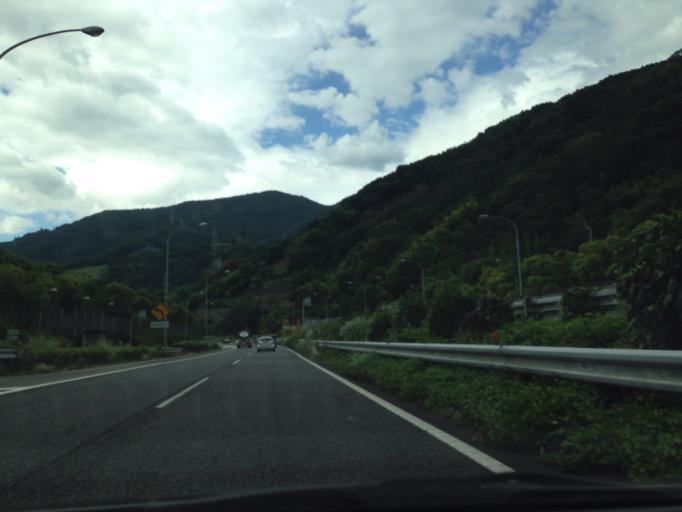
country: JP
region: Kanagawa
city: Hadano
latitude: 35.3636
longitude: 139.1020
